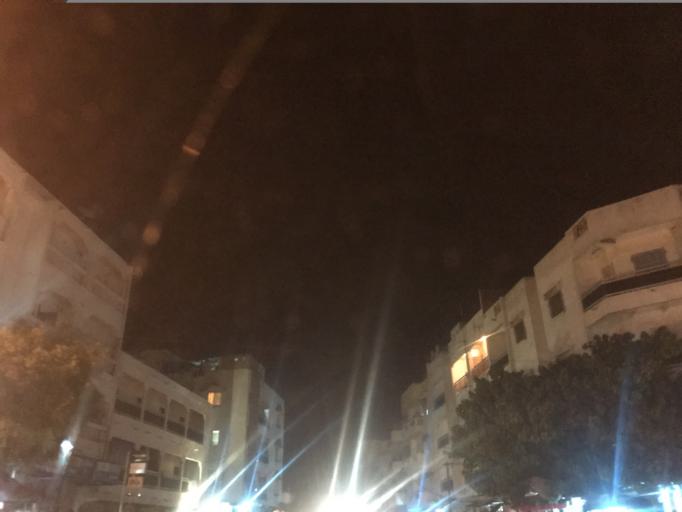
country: SN
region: Dakar
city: Grand Dakar
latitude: 14.7504
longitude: -17.4508
